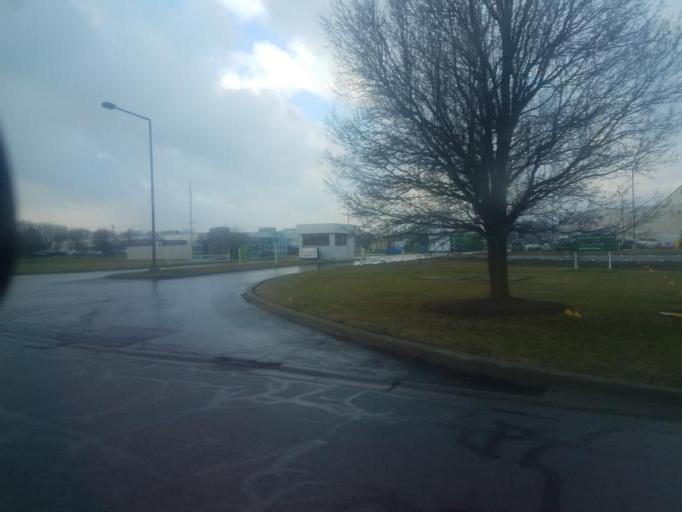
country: US
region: Ohio
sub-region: Marion County
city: Marion
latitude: 40.6097
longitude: -83.1409
